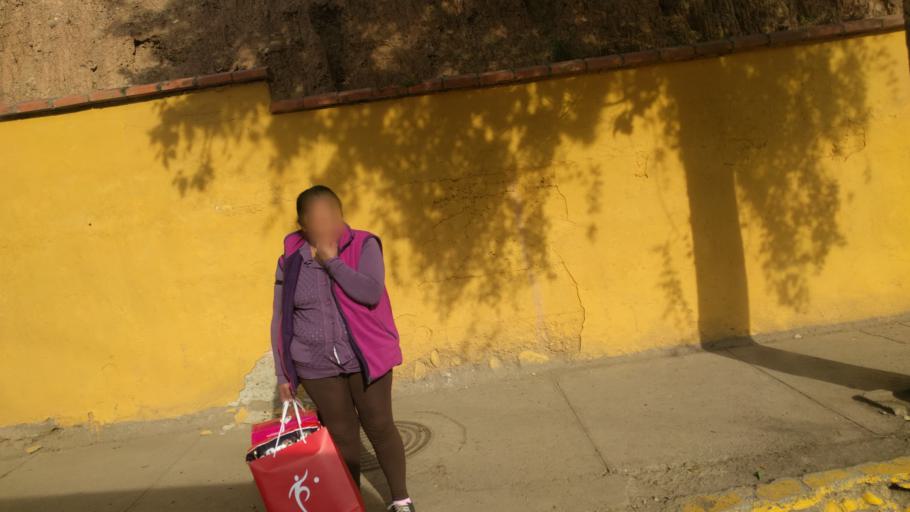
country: BO
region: La Paz
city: La Paz
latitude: -16.5592
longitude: -68.0940
